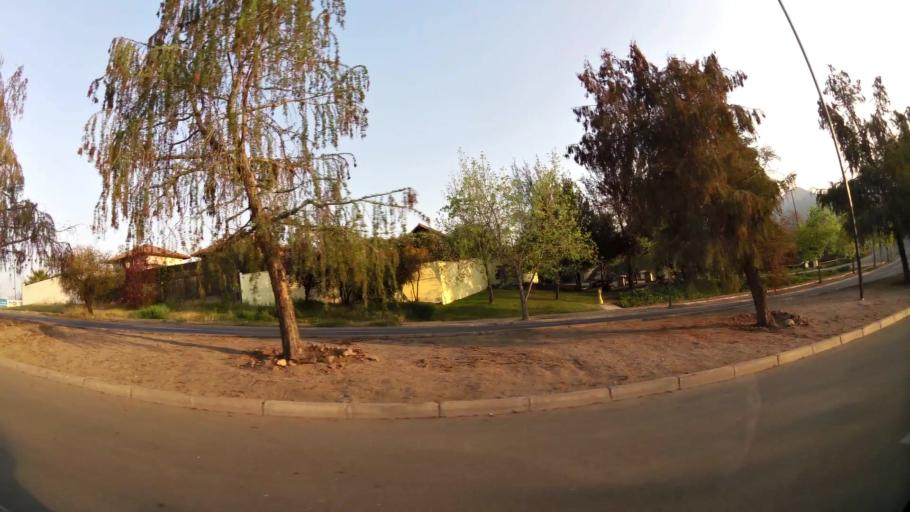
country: CL
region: Santiago Metropolitan
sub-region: Provincia de Chacabuco
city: Chicureo Abajo
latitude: -33.3237
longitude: -70.5395
